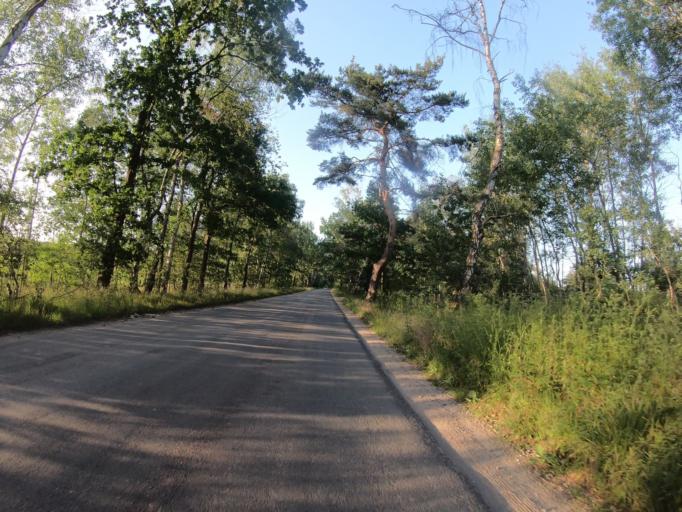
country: DE
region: Lower Saxony
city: Wagenhoff
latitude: 52.5280
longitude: 10.4848
